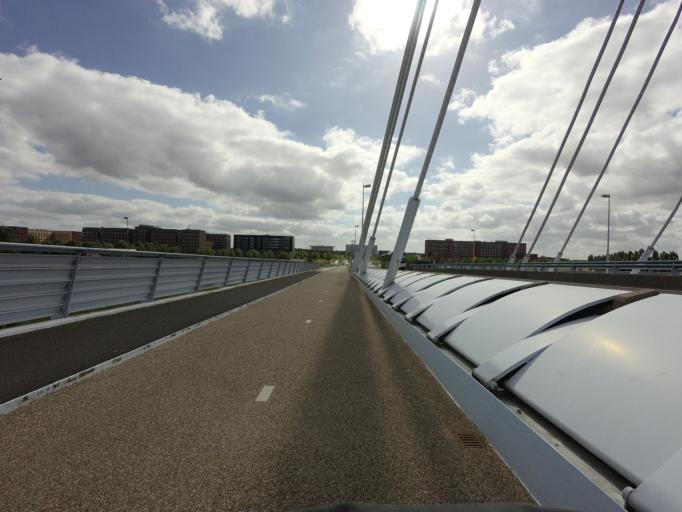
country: NL
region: Utrecht
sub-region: Gemeente Utrecht
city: Utrecht
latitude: 52.0704
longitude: 5.0868
